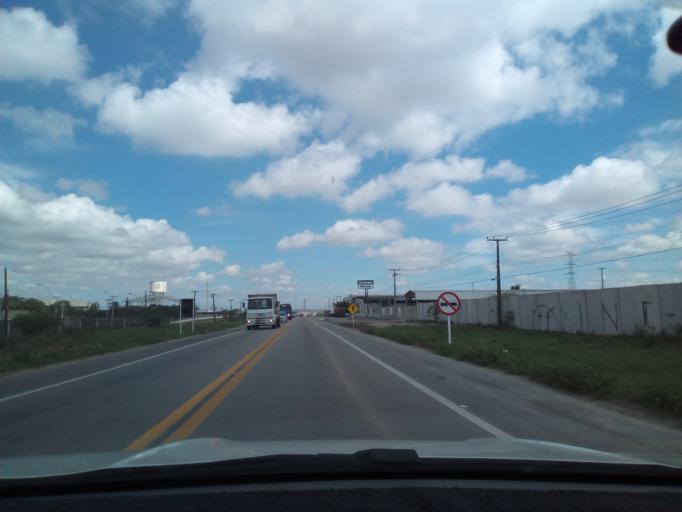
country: BR
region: Paraiba
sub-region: Campina Grande
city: Campina Grande
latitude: -7.2773
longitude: -35.8995
